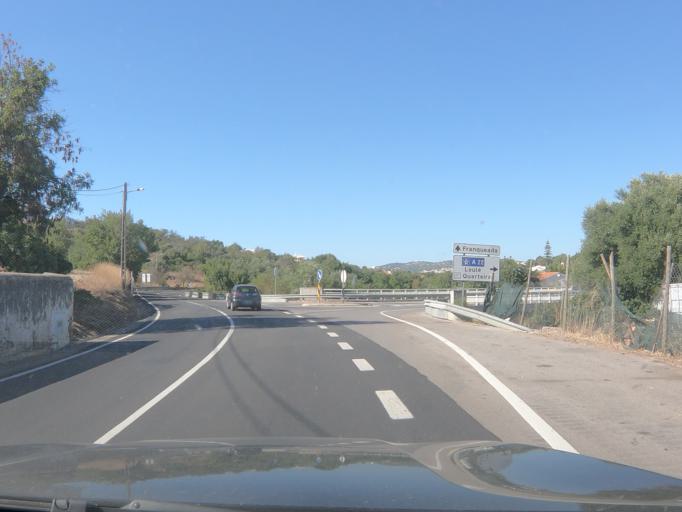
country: PT
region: Faro
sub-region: Loule
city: Almancil
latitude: 37.1056
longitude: -8.0519
